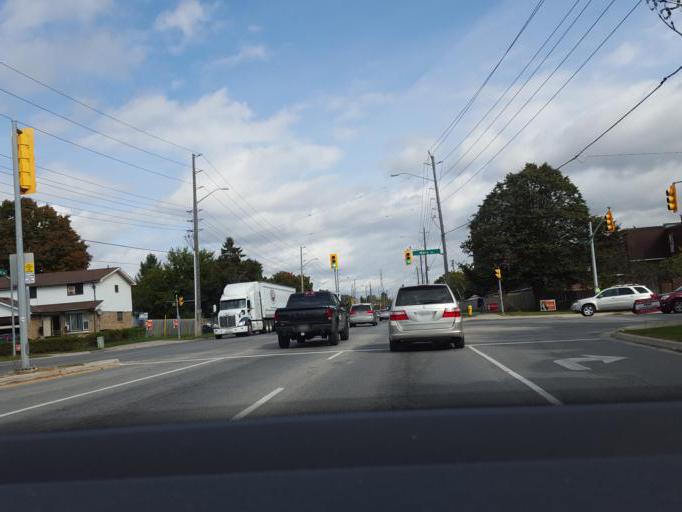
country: CA
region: Ontario
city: Oshawa
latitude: 43.9340
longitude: -78.8732
